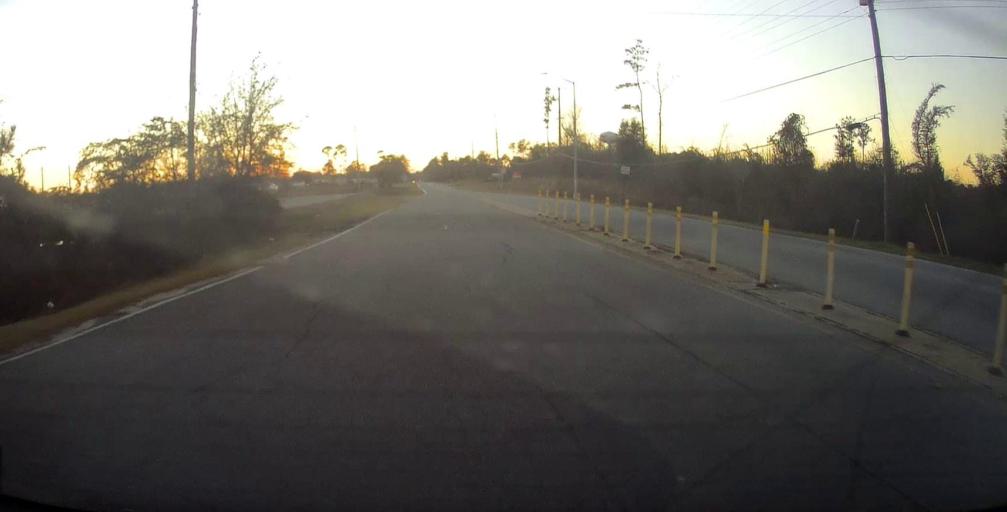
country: US
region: Georgia
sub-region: Dougherty County
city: Putney
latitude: 31.5292
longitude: -84.1164
